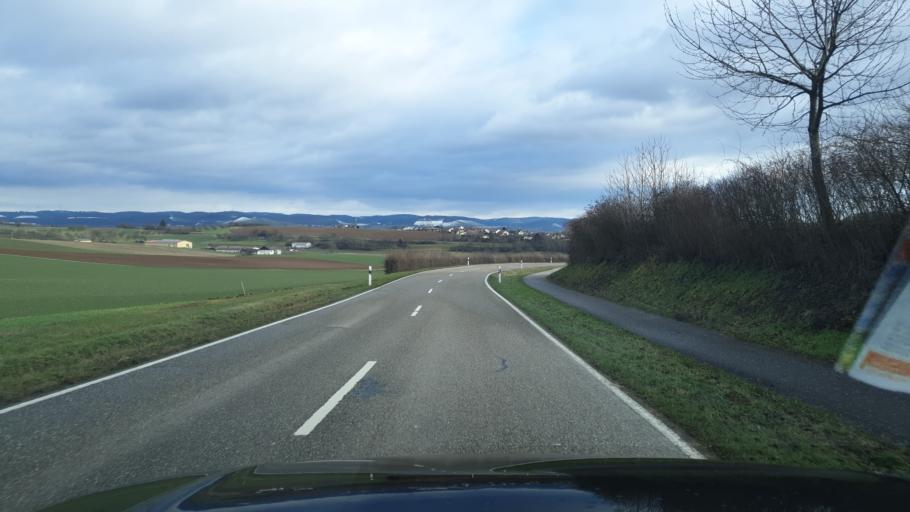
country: DE
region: Baden-Wuerttemberg
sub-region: Regierungsbezirk Stuttgart
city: Ilsfeld
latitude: 49.0624
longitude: 9.2276
